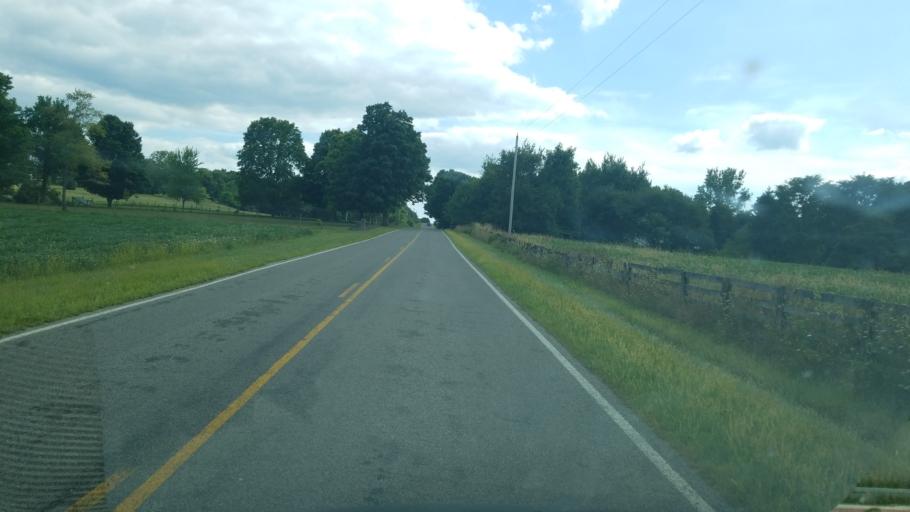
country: US
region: Ohio
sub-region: Logan County
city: De Graff
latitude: 40.2678
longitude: -83.9266
